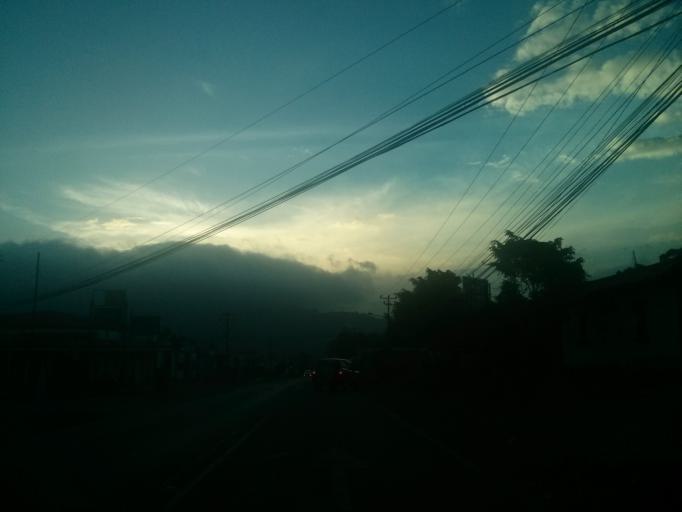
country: CR
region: Cartago
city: Cartago
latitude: 9.8775
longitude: -83.9278
